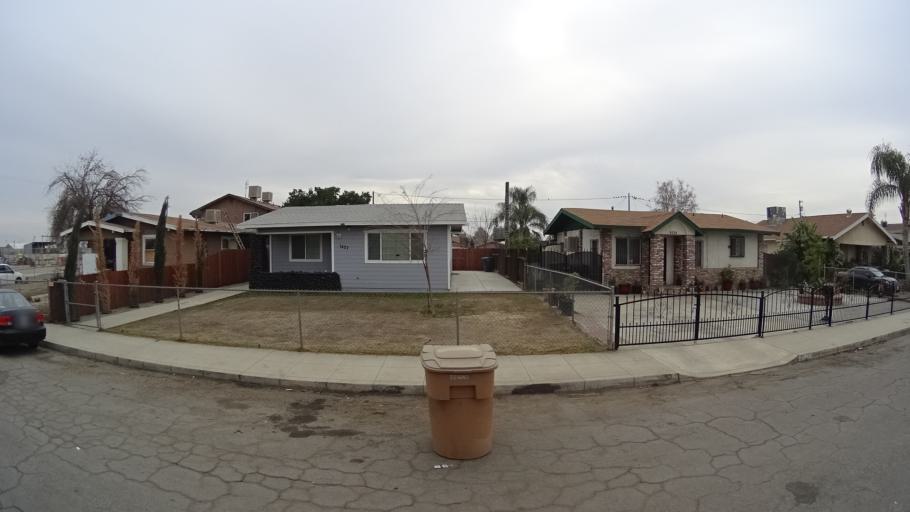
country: US
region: California
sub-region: Kern County
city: Bakersfield
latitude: 35.3709
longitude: -118.9821
